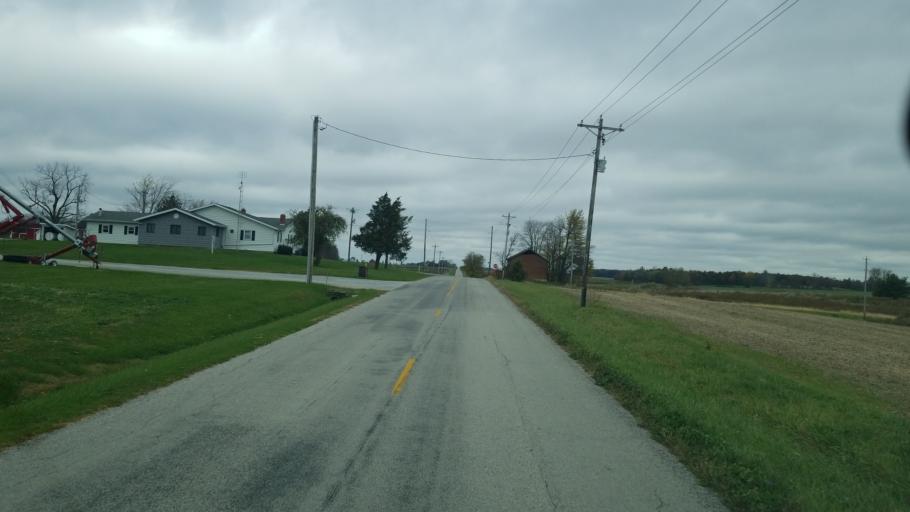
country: US
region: Ohio
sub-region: Sandusky County
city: Mount Carmel
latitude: 41.0797
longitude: -82.9575
